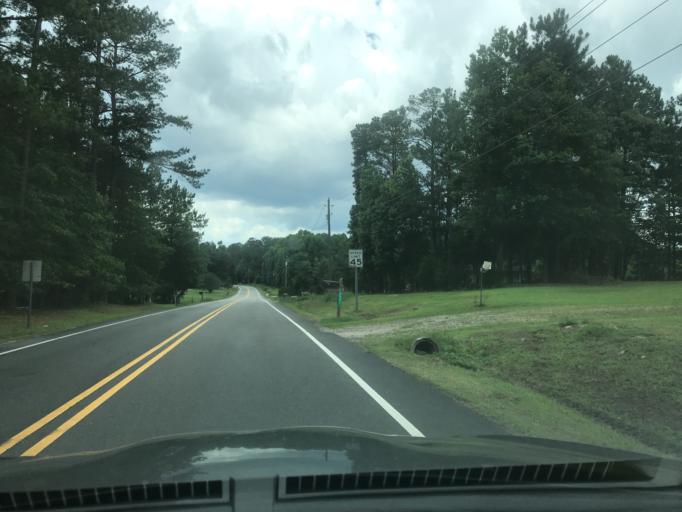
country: US
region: North Carolina
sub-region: Wake County
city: Knightdale
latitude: 35.8352
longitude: -78.4739
